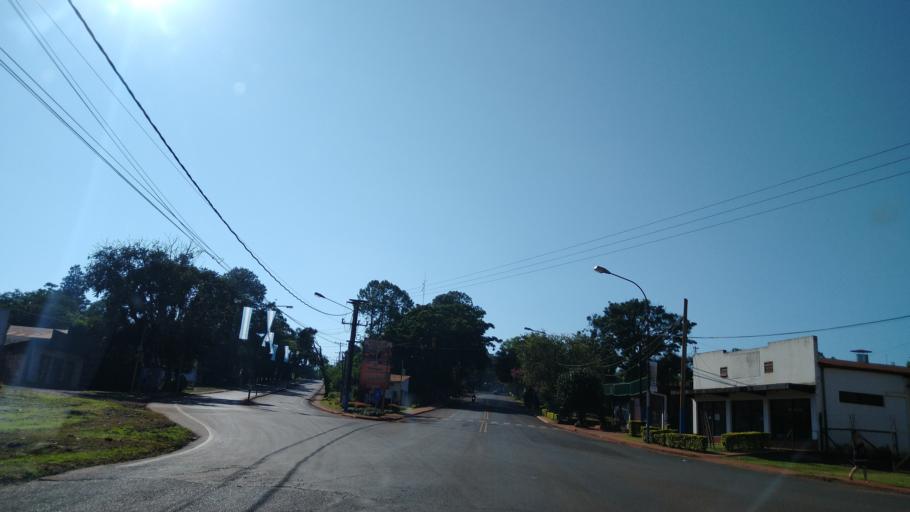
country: AR
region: Misiones
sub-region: Departamento de Montecarlo
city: Montecarlo
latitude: -26.5716
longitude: -54.7416
